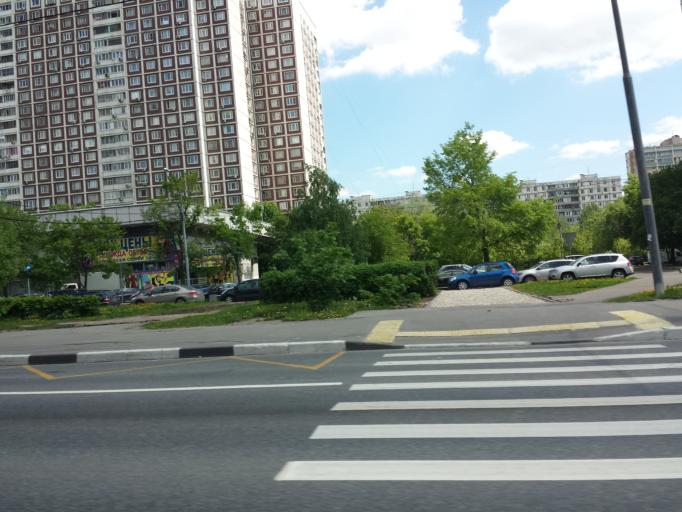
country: RU
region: Moscow
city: Lianozovo
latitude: 55.8939
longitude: 37.5870
